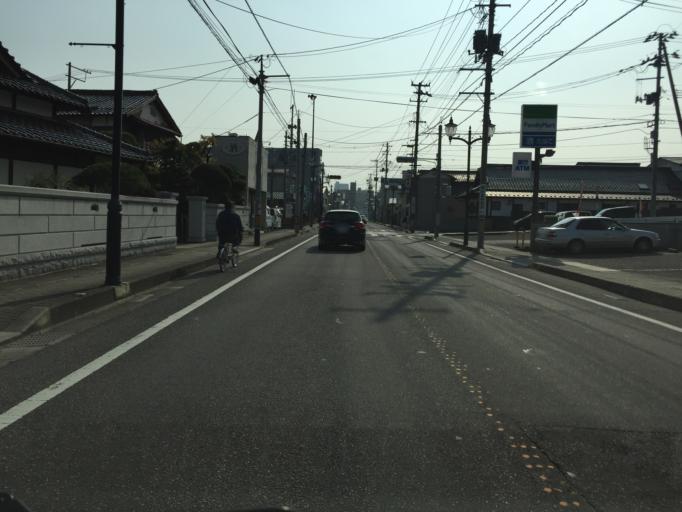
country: JP
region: Fukushima
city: Koriyama
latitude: 37.4109
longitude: 140.3910
